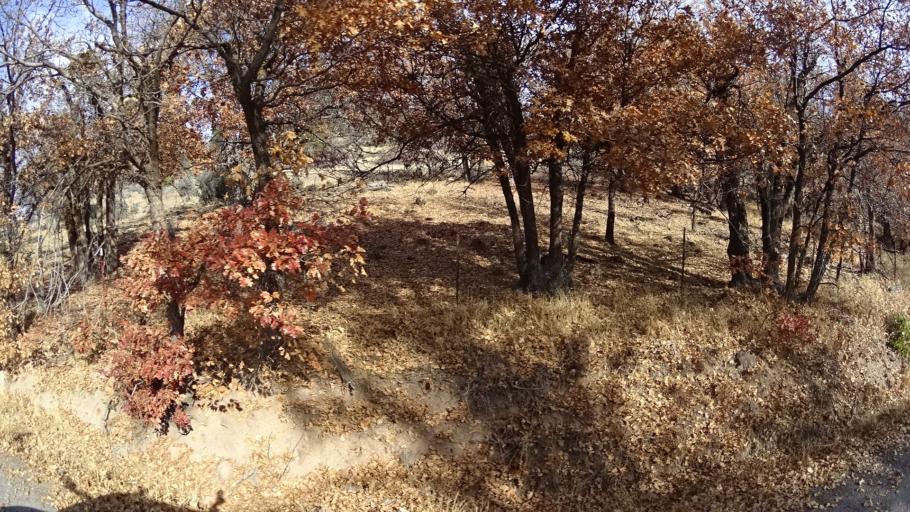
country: US
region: California
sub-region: Siskiyou County
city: Weed
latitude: 41.4461
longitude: -122.4254
